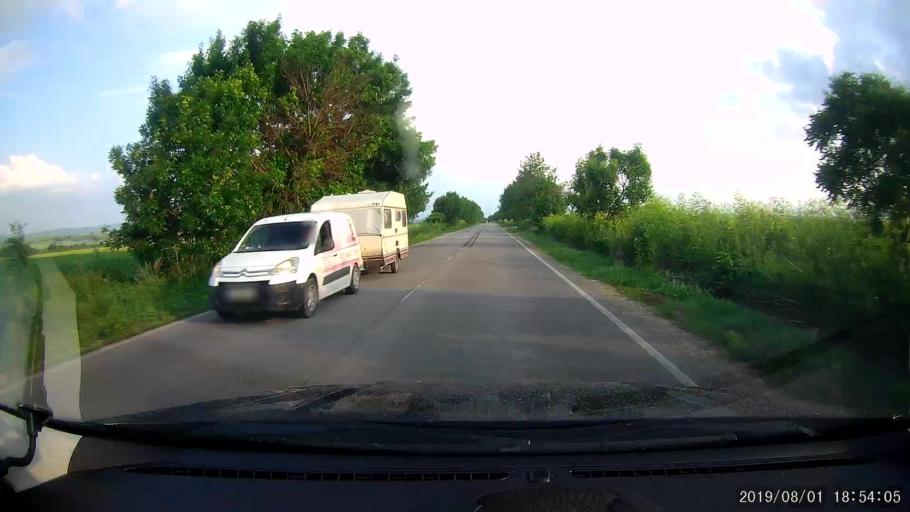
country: BG
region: Shumen
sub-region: Obshtina Shumen
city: Shumen
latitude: 43.2074
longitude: 26.9994
